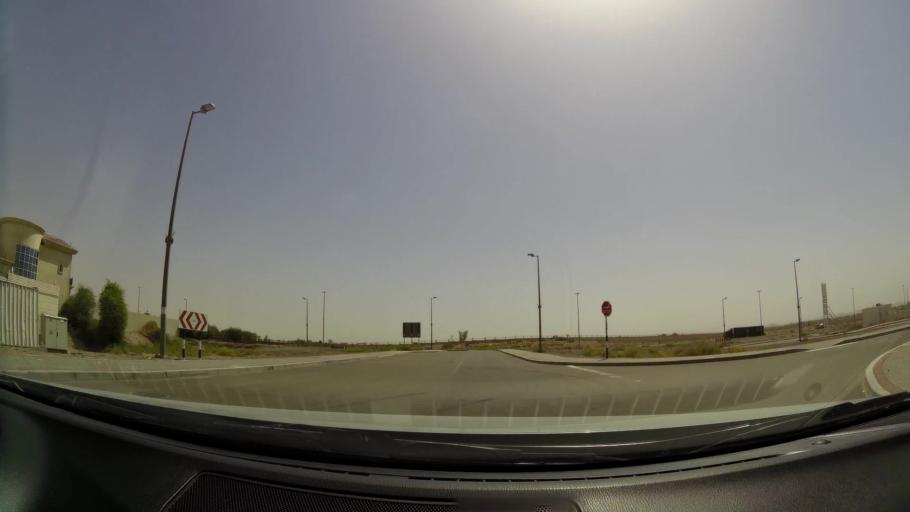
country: OM
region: Al Buraimi
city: Al Buraymi
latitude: 24.3125
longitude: 55.7561
